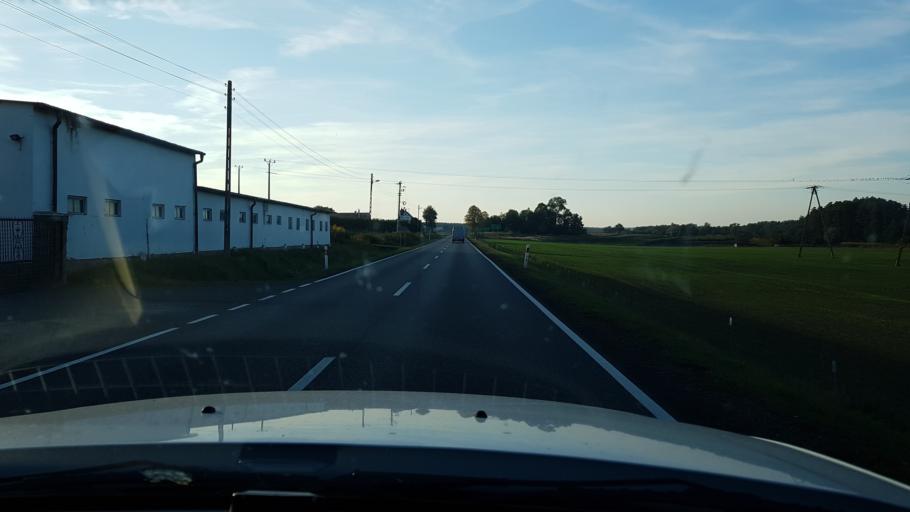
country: PL
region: West Pomeranian Voivodeship
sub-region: Powiat gryfinski
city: Chojna
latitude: 52.9637
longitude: 14.4085
